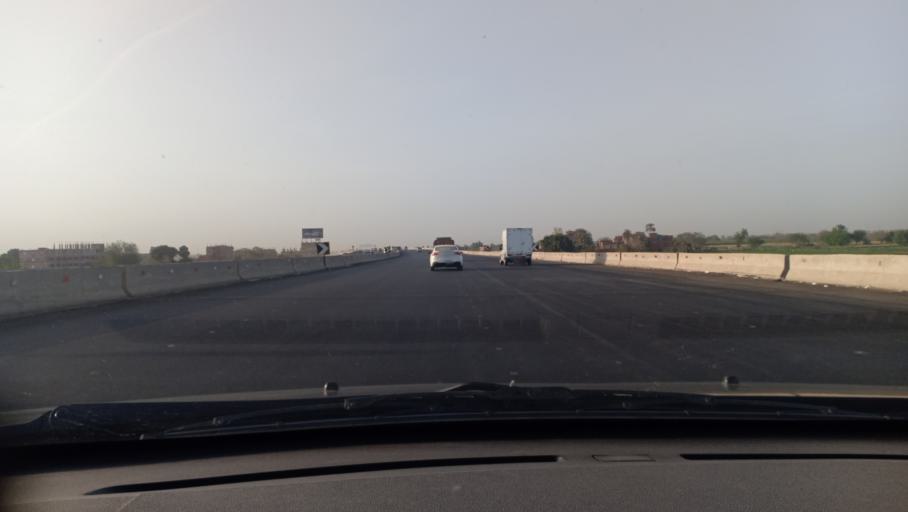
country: EG
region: Muhafazat al Qalyubiyah
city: Qalyub
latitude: 30.2177
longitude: 31.2260
